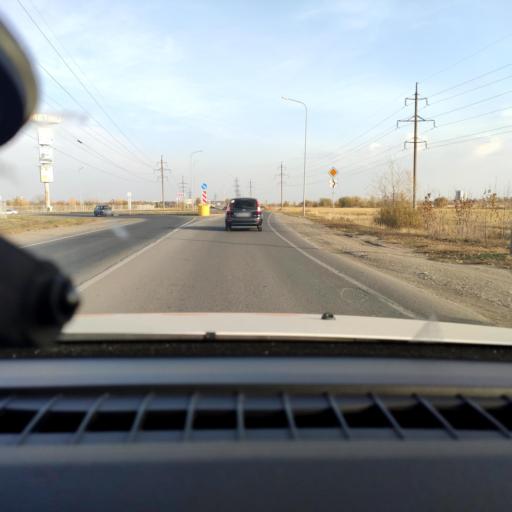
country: RU
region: Samara
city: Samara
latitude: 53.1324
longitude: 50.1375
